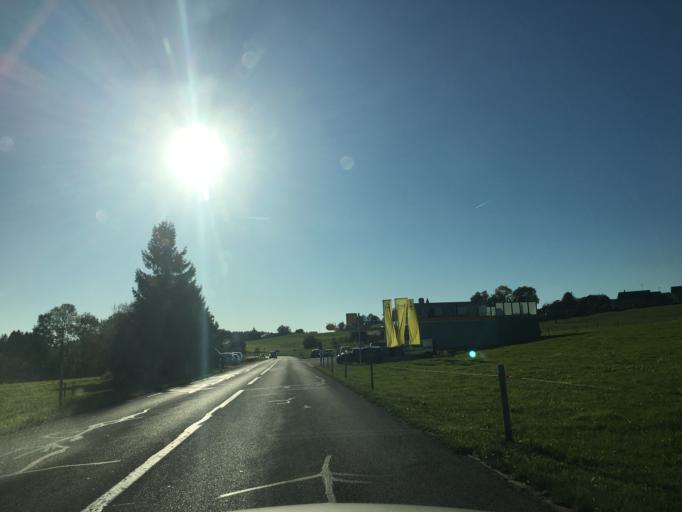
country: CH
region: Fribourg
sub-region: Gruyere District
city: Sales
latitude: 46.6079
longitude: 6.9140
